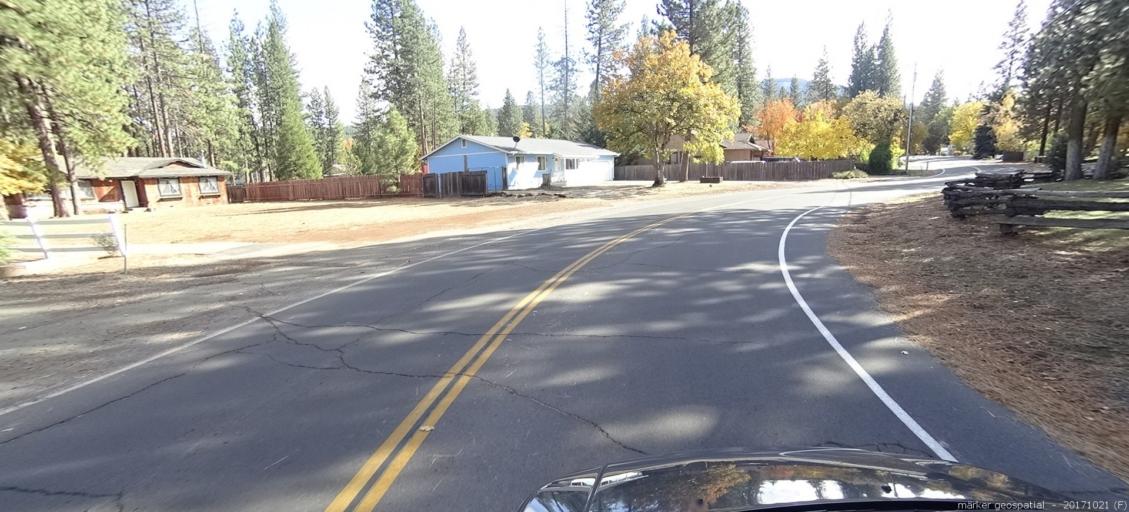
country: US
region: California
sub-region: Shasta County
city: Burney
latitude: 40.8821
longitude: -121.6574
